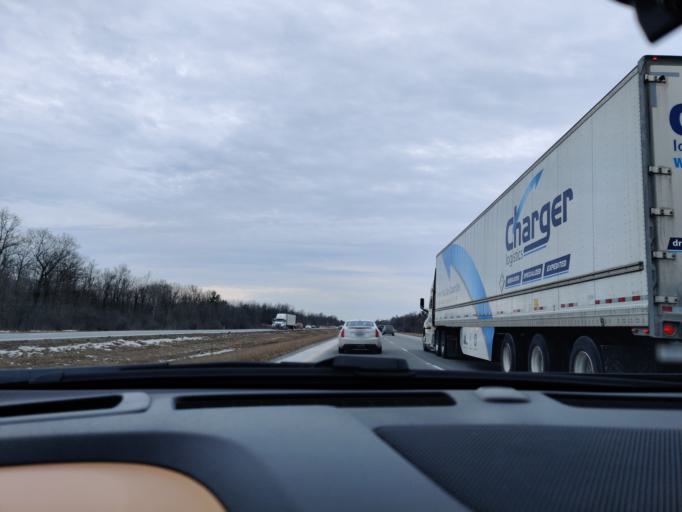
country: CA
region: Ontario
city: Prescott
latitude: 44.6823
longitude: -75.5912
